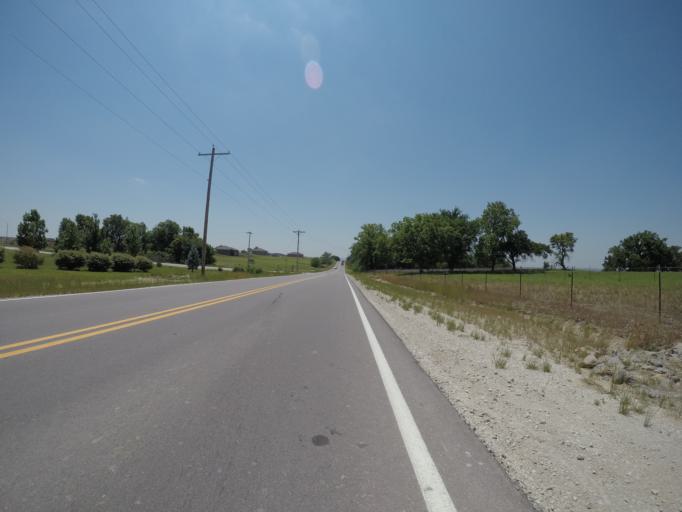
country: US
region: Kansas
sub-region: Riley County
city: Manhattan
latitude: 39.2110
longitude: -96.4405
